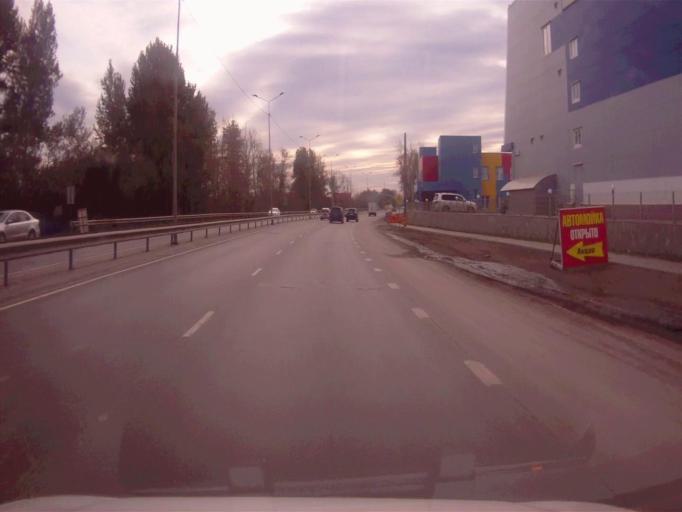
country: RU
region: Chelyabinsk
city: Novosineglazovskiy
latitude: 55.0885
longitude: 61.3989
